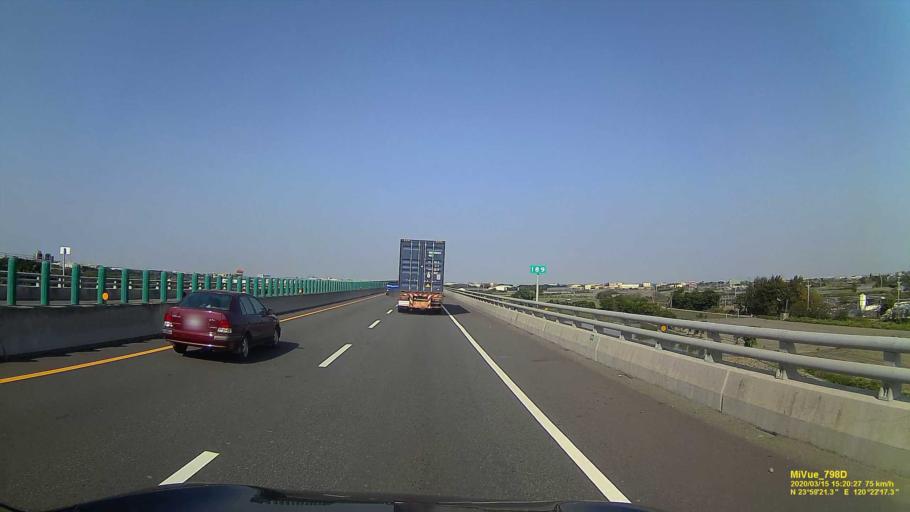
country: TW
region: Taiwan
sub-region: Changhua
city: Chang-hua
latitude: 23.9904
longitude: 120.3723
